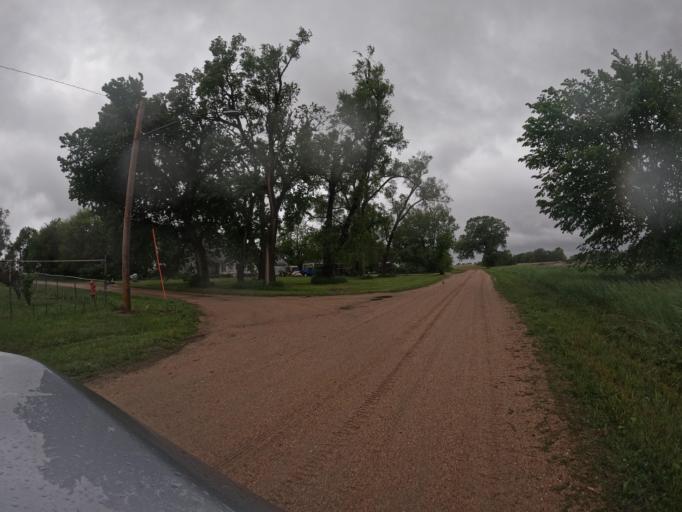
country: US
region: Nebraska
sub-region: Clay County
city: Harvard
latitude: 40.6165
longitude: -98.1011
